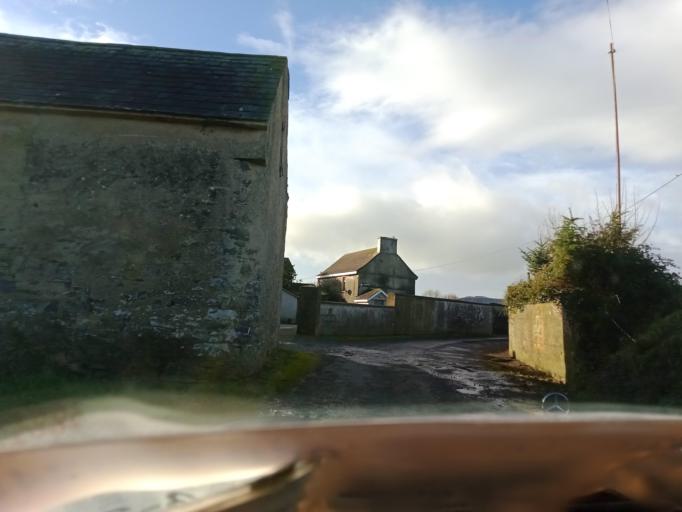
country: IE
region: Leinster
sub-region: Kilkenny
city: Mooncoin
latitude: 52.2767
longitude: -7.2582
